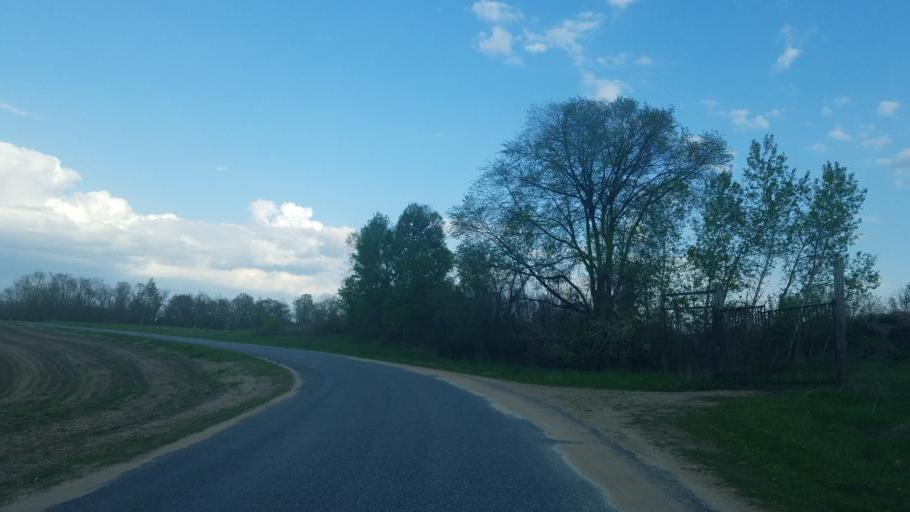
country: US
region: Wisconsin
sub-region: Vernon County
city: Hillsboro
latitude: 43.6756
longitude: -90.3677
